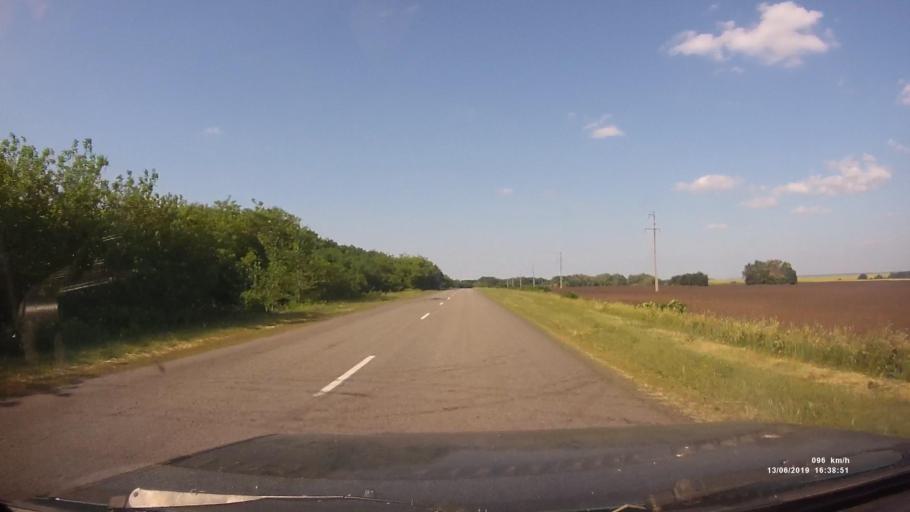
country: RU
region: Rostov
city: Kazanskaya
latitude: 49.9230
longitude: 41.3301
